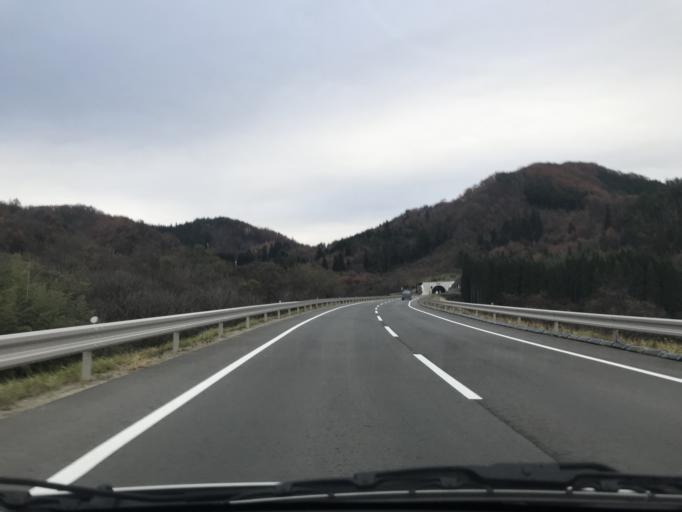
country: JP
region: Iwate
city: Kitakami
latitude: 39.2846
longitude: 141.2361
